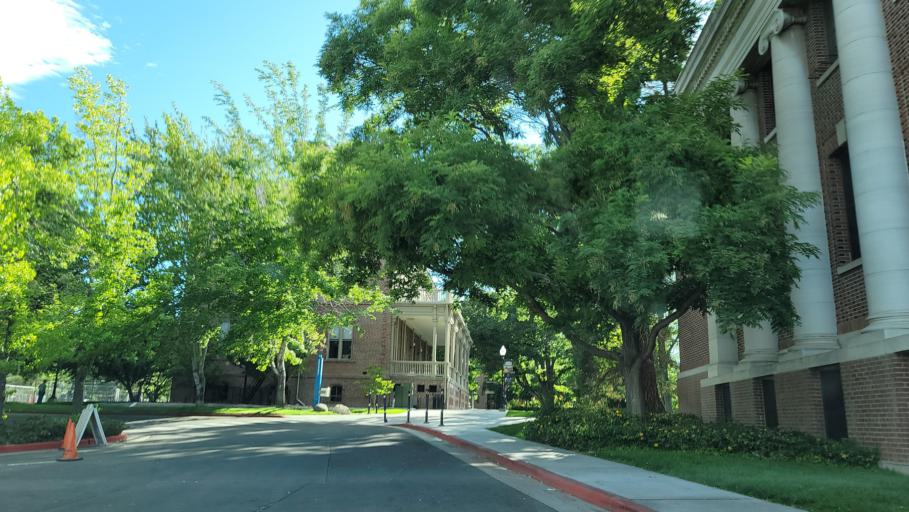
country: US
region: Nevada
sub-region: Washoe County
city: Reno
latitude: 39.5379
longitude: -119.8133
